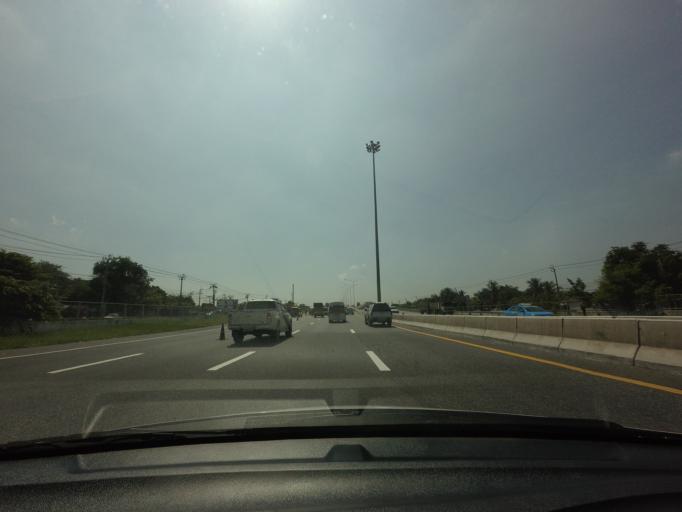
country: TH
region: Bangkok
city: Lat Krabang
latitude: 13.7172
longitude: 100.8167
